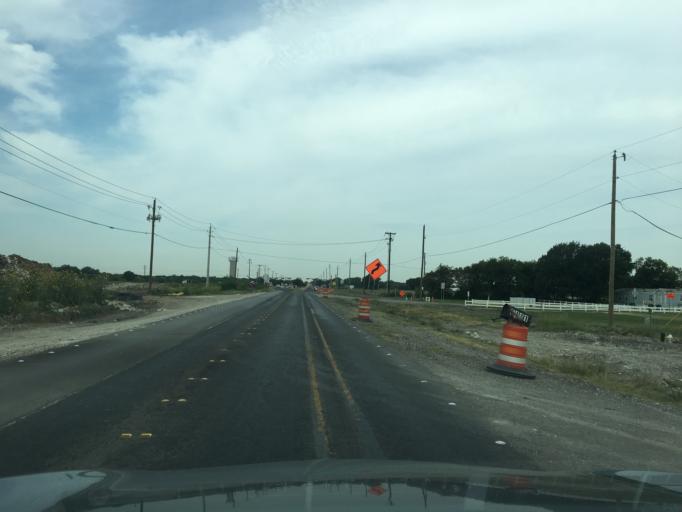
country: US
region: Texas
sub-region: Collin County
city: Parker
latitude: 33.0553
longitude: -96.6078
